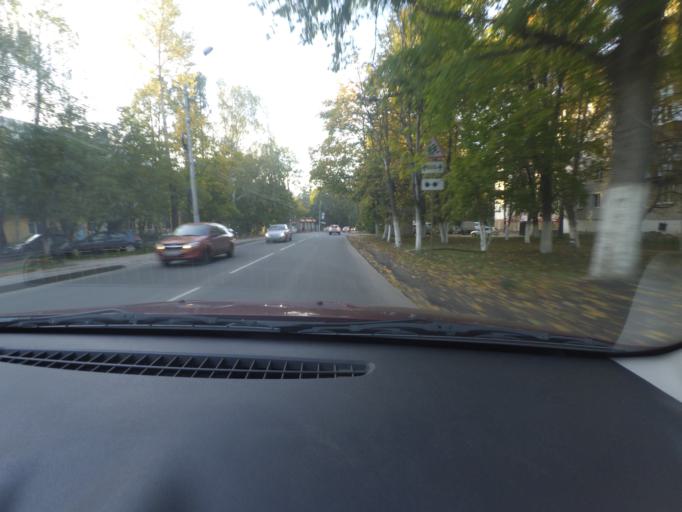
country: RU
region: Nizjnij Novgorod
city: Nizhniy Novgorod
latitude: 56.2624
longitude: 44.0009
